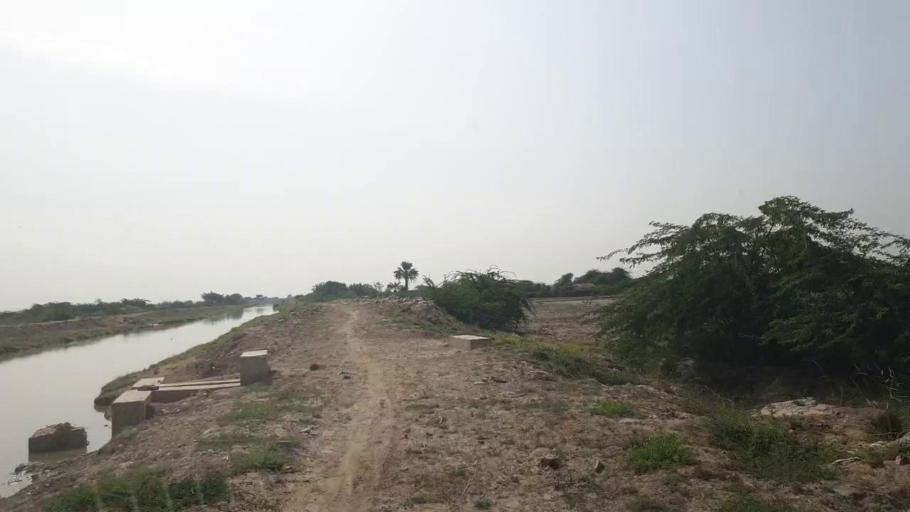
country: PK
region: Sindh
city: Badin
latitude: 24.5623
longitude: 68.8499
